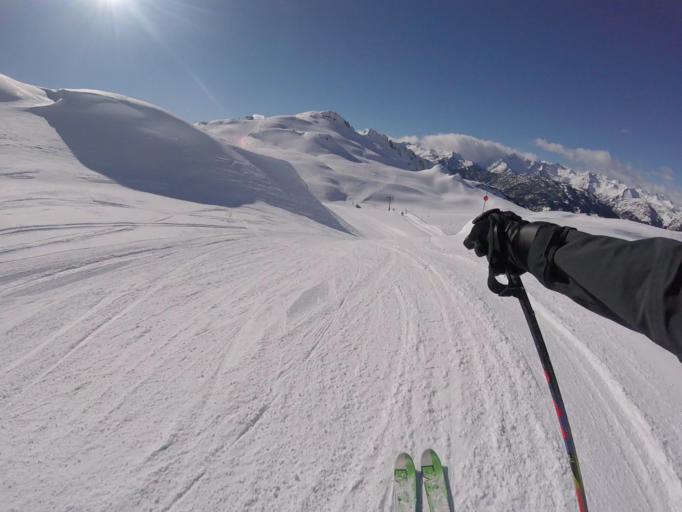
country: ES
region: Catalonia
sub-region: Provincia de Lleida
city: Vielha
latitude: 42.7269
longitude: 0.9396
